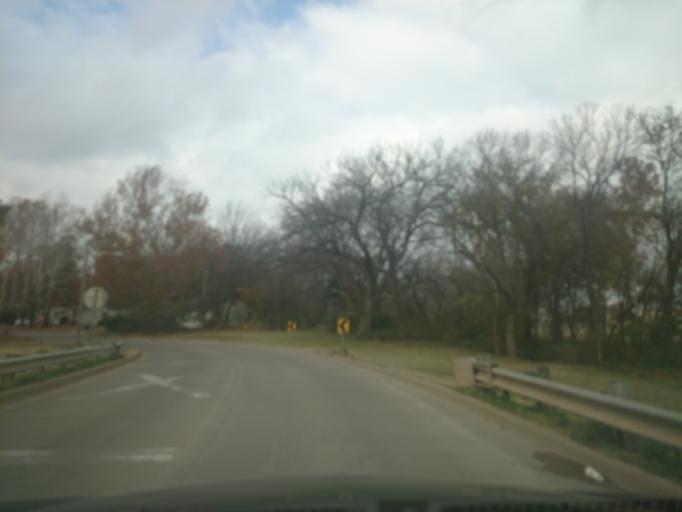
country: US
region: Oklahoma
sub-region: Payne County
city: Stillwater
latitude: 36.1236
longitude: -97.0553
